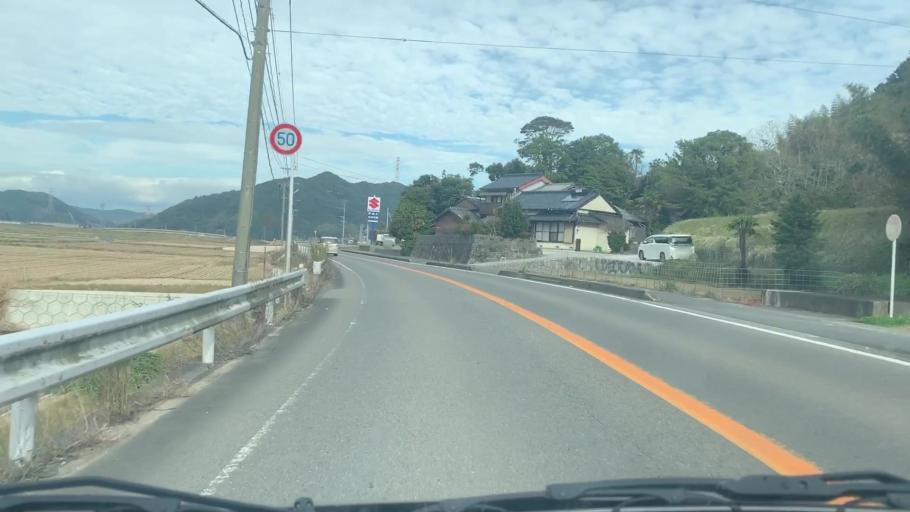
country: JP
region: Saga Prefecture
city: Karatsu
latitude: 33.3678
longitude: 130.0049
